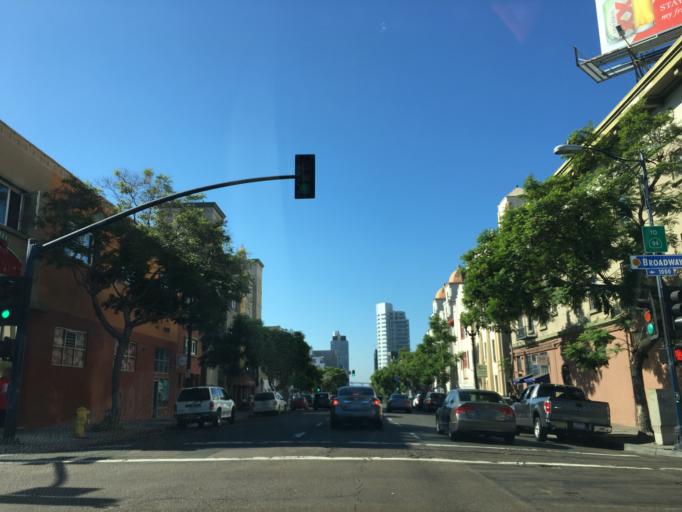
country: US
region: California
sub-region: San Diego County
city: San Diego
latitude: 32.7159
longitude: -117.1556
